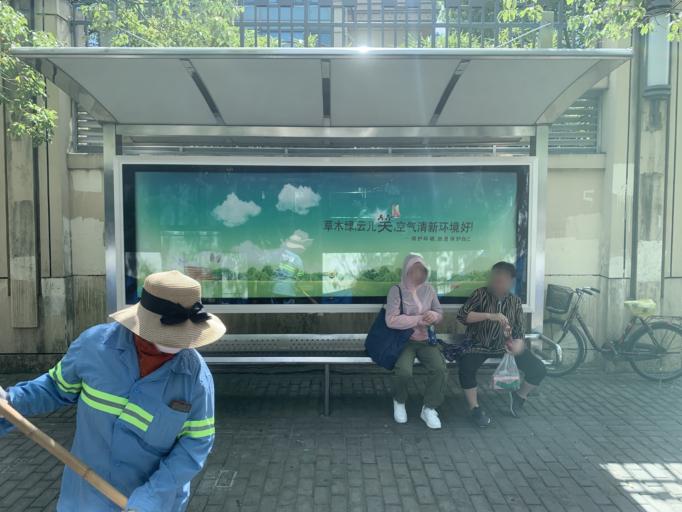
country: CN
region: Shanghai Shi
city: Huamu
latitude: 31.1795
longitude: 121.5335
